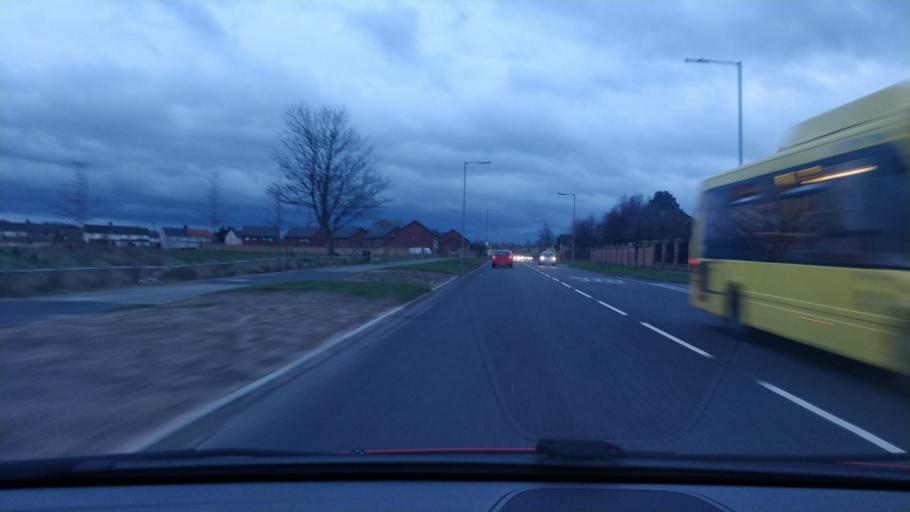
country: GB
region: England
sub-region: Knowsley
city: Kirkby
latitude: 53.4551
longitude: -2.9072
